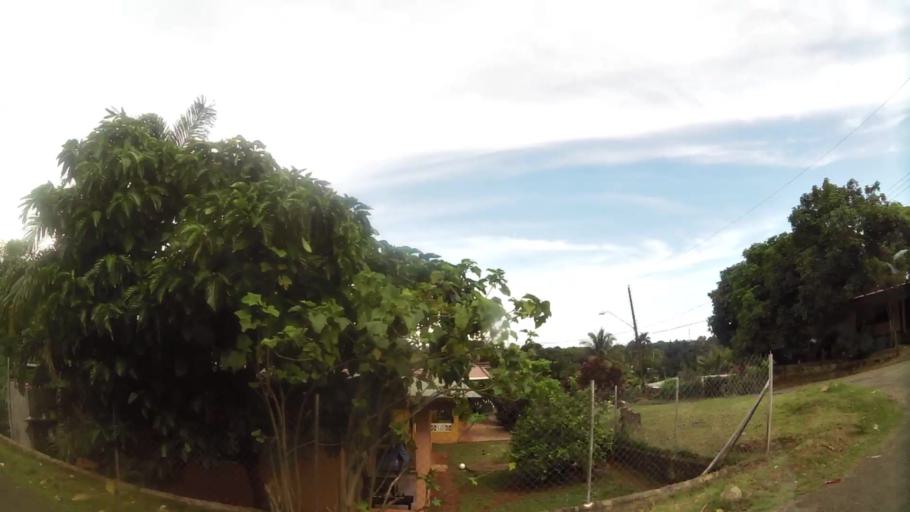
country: PA
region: Panama
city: Guadalupe
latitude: 8.8606
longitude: -79.8127
